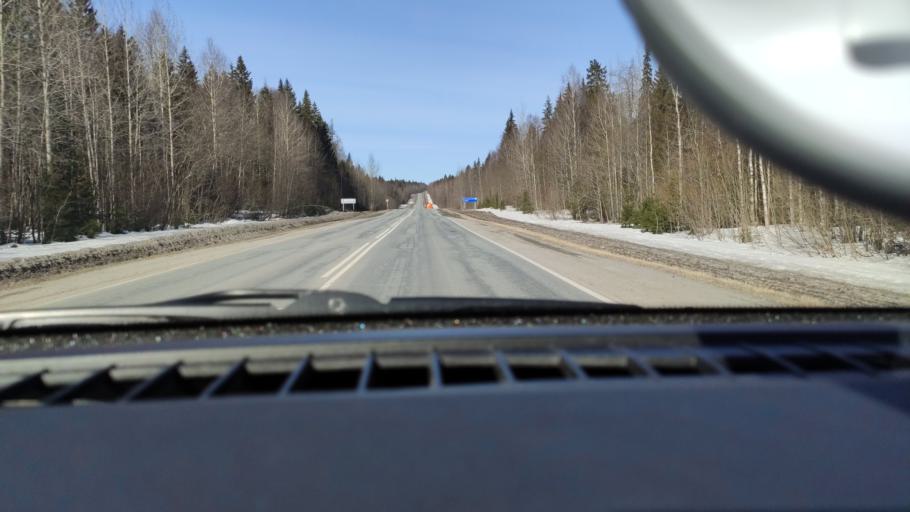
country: RU
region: Perm
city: Perm
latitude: 58.1586
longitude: 56.2480
